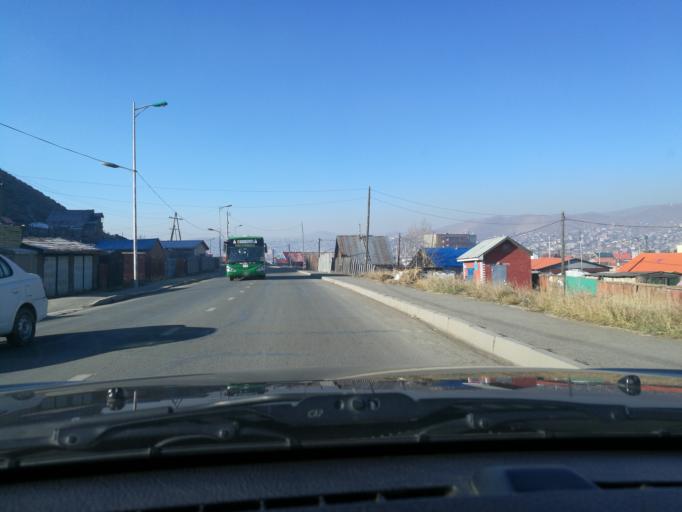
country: MN
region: Ulaanbaatar
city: Ulaanbaatar
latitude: 47.9770
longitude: 106.9359
